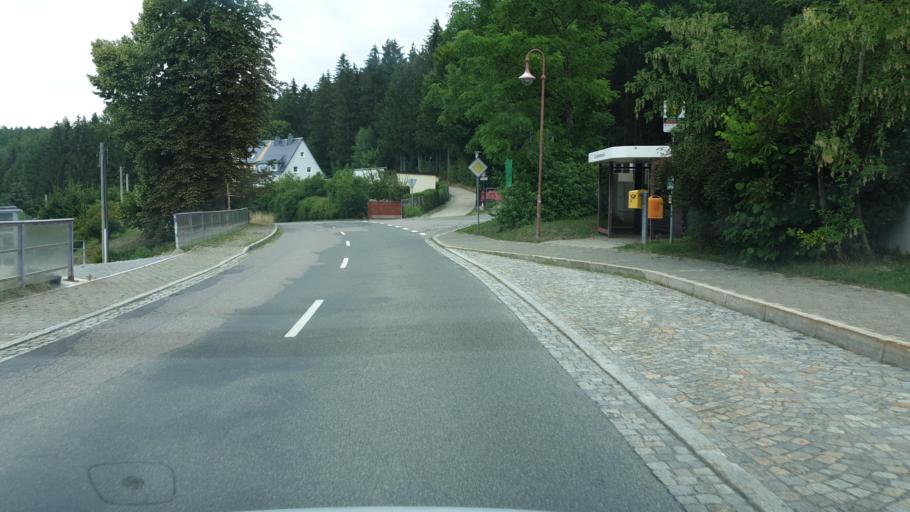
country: DE
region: Saxony
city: Bernsbach
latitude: 50.5888
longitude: 12.7485
